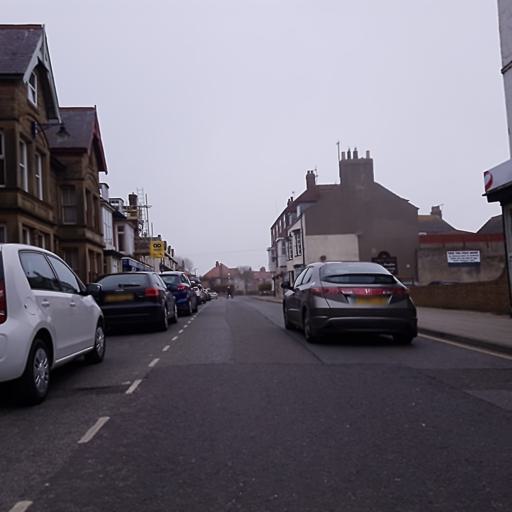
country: GB
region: England
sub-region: North Yorkshire
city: Filey
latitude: 54.2085
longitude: -0.2878
